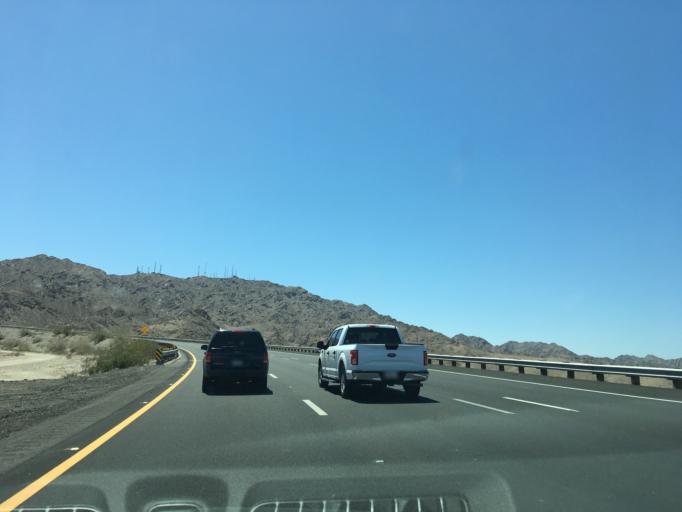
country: US
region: Arizona
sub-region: Yuma County
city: Fortuna Foothills
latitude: 32.6735
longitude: -114.3078
